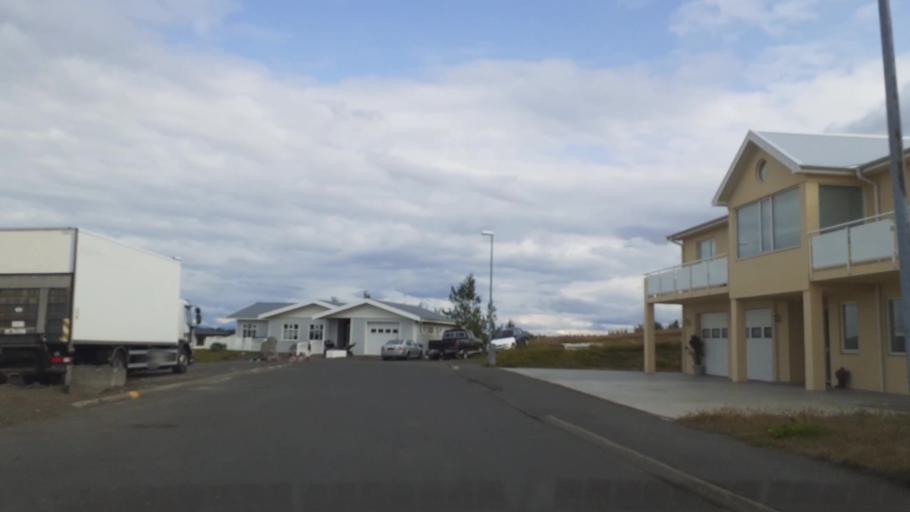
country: IS
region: South
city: Vestmannaeyjar
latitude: 63.7551
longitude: -20.2135
